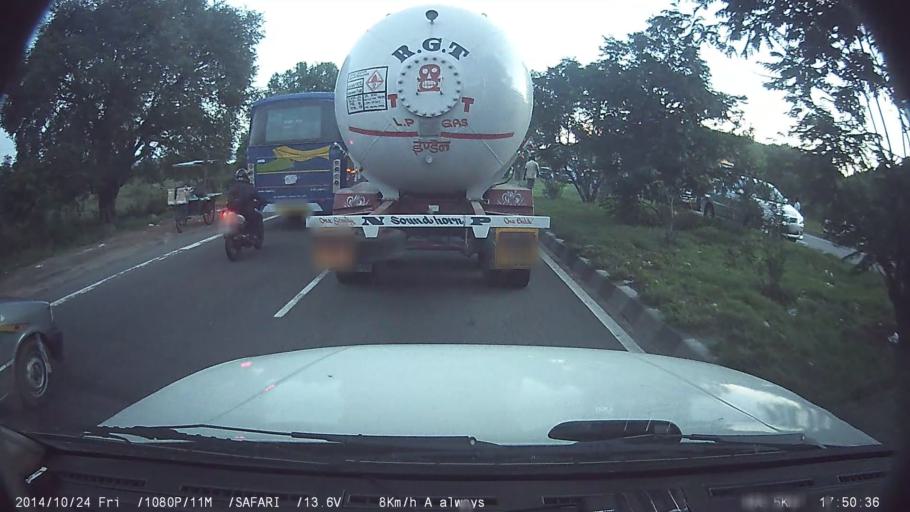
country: IN
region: Tamil Nadu
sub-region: Kancheepuram
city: Chengalpattu
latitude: 12.7207
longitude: 79.9813
